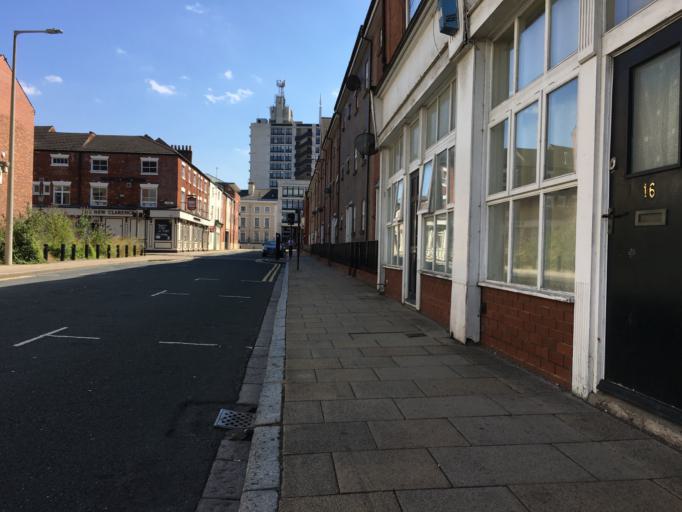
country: GB
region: England
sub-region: City of Kingston upon Hull
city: Hull
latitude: 53.7481
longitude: -0.3399
